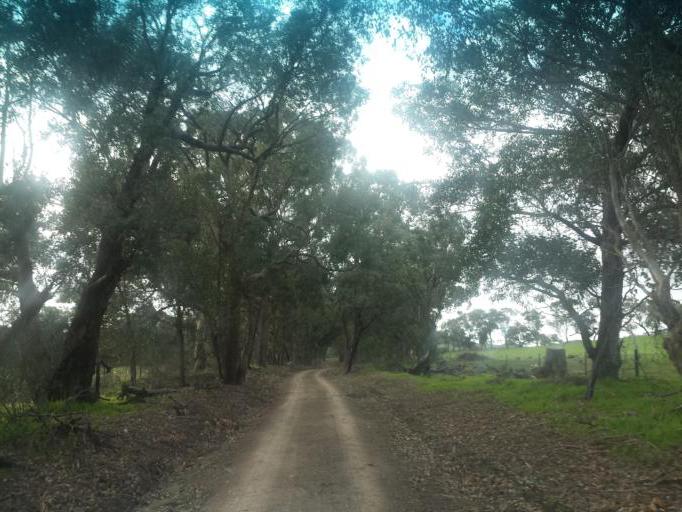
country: AU
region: Victoria
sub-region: Murrindindi
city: Kinglake West
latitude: -37.0168
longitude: 145.2502
